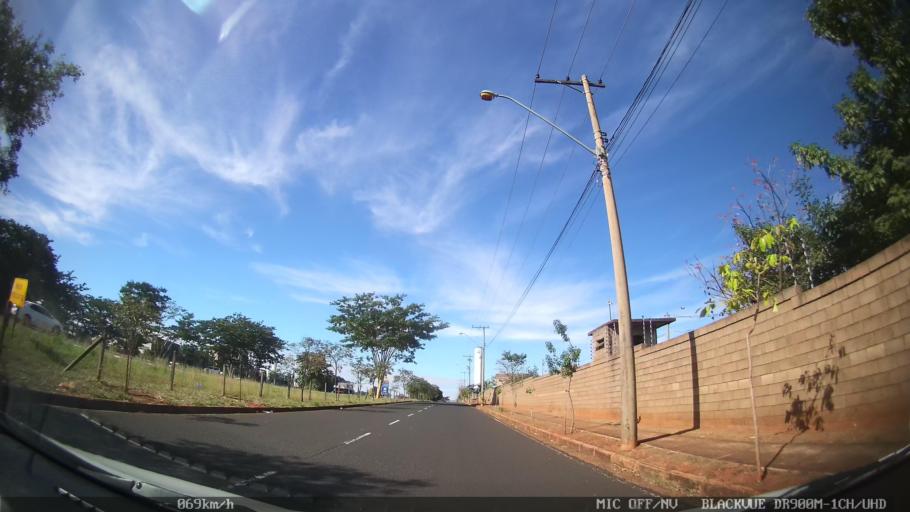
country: BR
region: Sao Paulo
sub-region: Sao Jose Do Rio Preto
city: Sao Jose do Rio Preto
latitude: -20.8010
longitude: -49.3408
